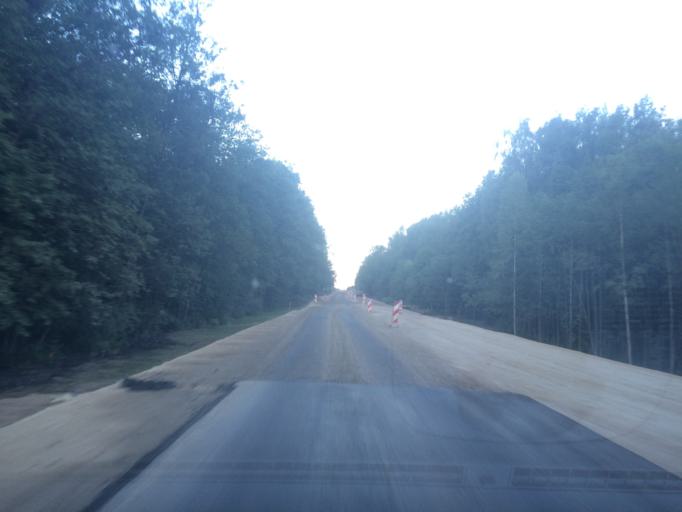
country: LT
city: Zarasai
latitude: 55.7584
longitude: 26.3289
